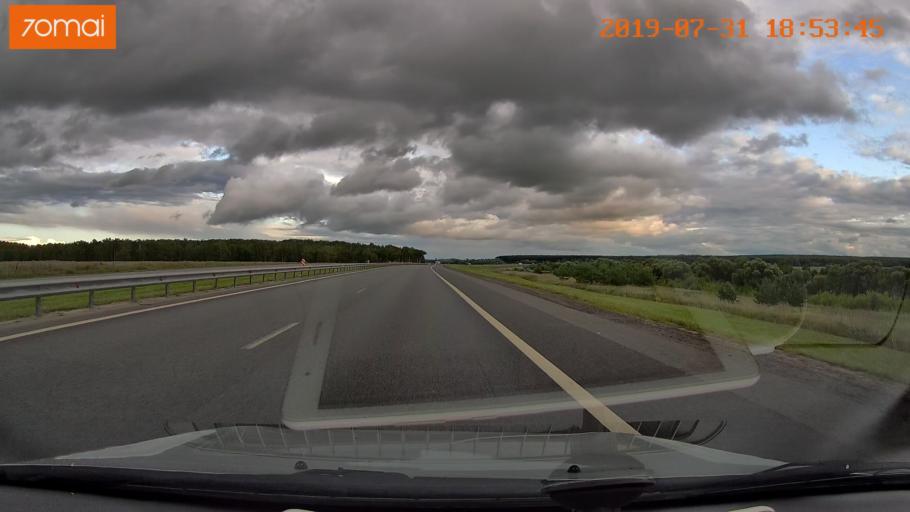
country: RU
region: Moskovskaya
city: Raduzhnyy
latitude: 55.1993
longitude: 38.6591
